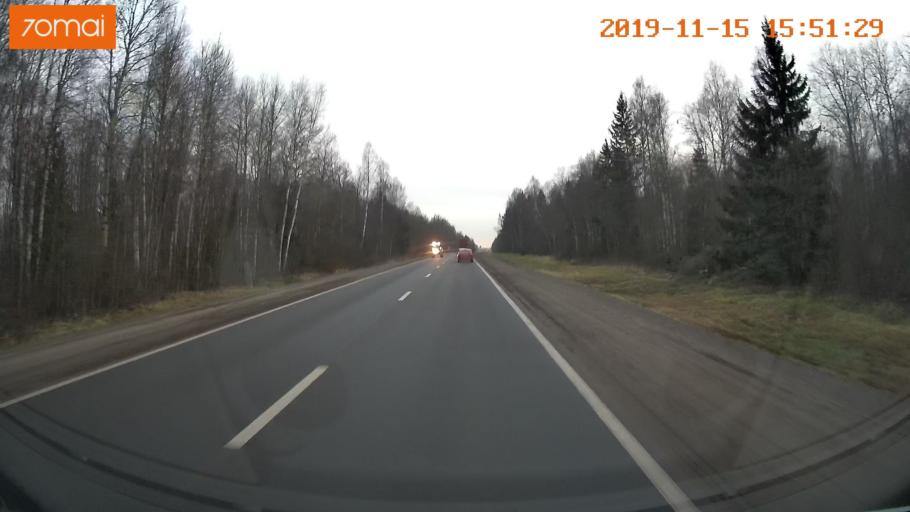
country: RU
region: Jaroslavl
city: Yaroslavl
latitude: 57.8937
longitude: 40.0070
